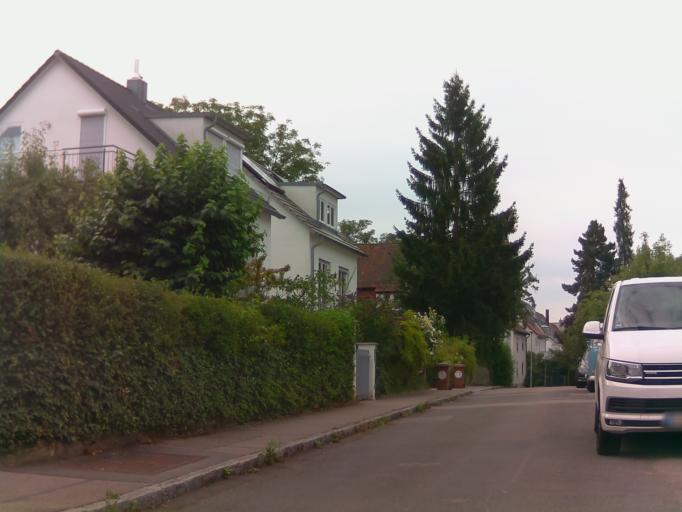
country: DE
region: Baden-Wuerttemberg
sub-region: Regierungsbezirk Stuttgart
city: Leinfelden-Echterdingen
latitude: 48.7310
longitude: 9.1207
